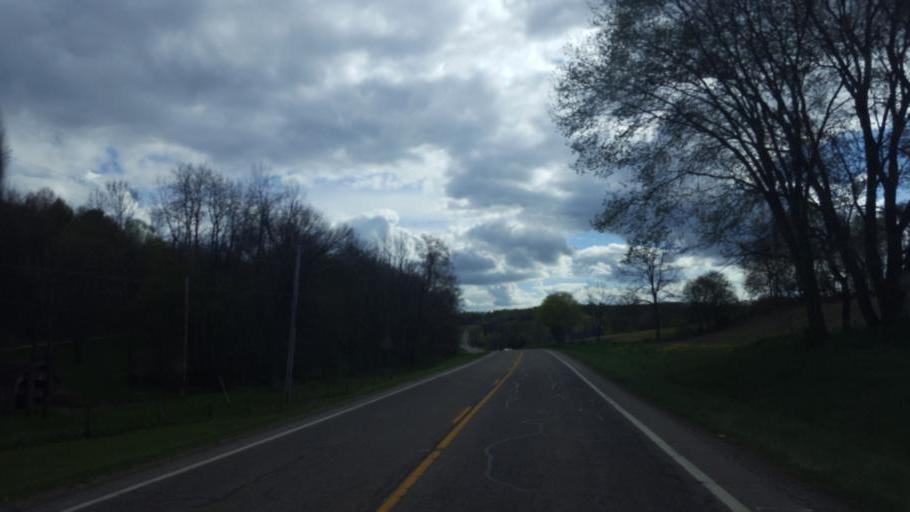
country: US
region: Ohio
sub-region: Knox County
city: Danville
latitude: 40.4931
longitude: -82.3502
